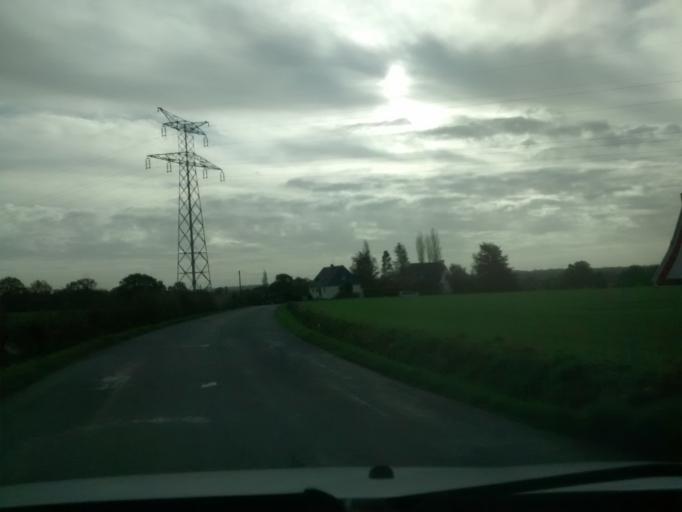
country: FR
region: Brittany
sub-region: Departement d'Ille-et-Vilaine
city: Servon-sur-Vilaine
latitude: 48.1276
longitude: -1.4775
